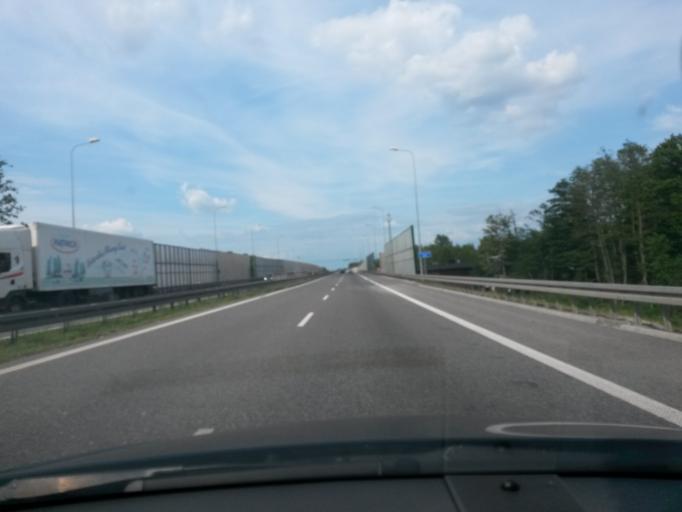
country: PL
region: Lodz Voivodeship
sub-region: Powiat skierniewicki
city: Kowiesy
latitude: 51.8882
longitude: 20.4179
